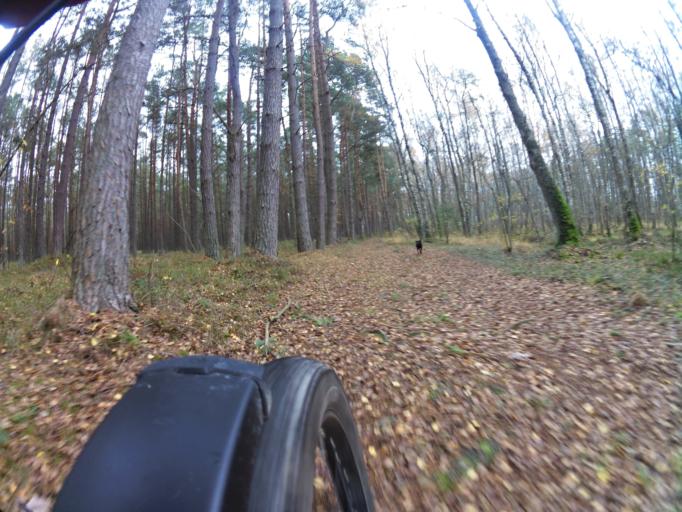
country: PL
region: Pomeranian Voivodeship
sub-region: Powiat leborski
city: Leba
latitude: 54.7670
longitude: 17.6000
